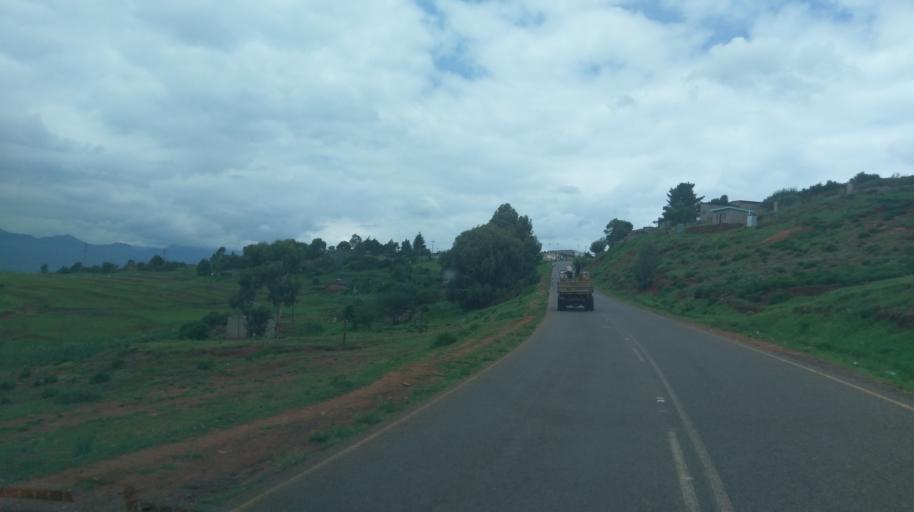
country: LS
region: Leribe
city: Leribe
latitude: -28.9988
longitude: 28.2058
